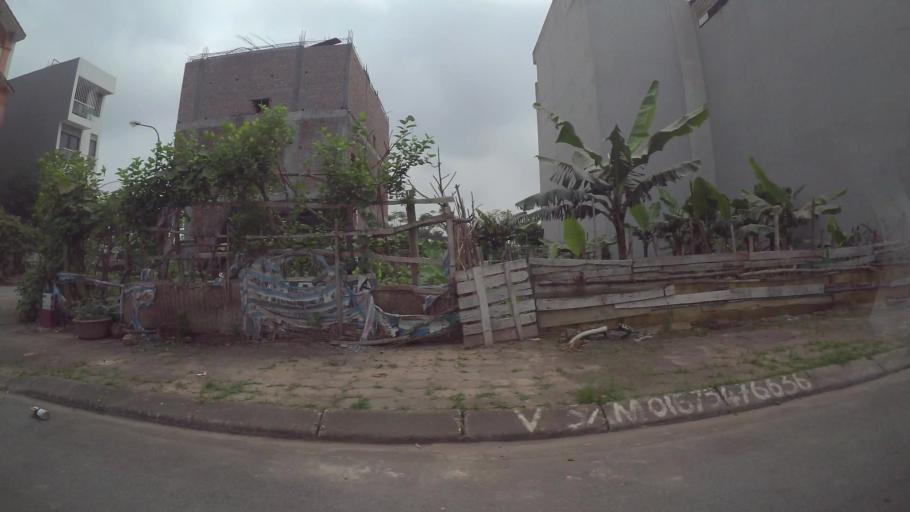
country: VN
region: Ha Noi
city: Trau Quy
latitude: 21.0645
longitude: 105.9168
